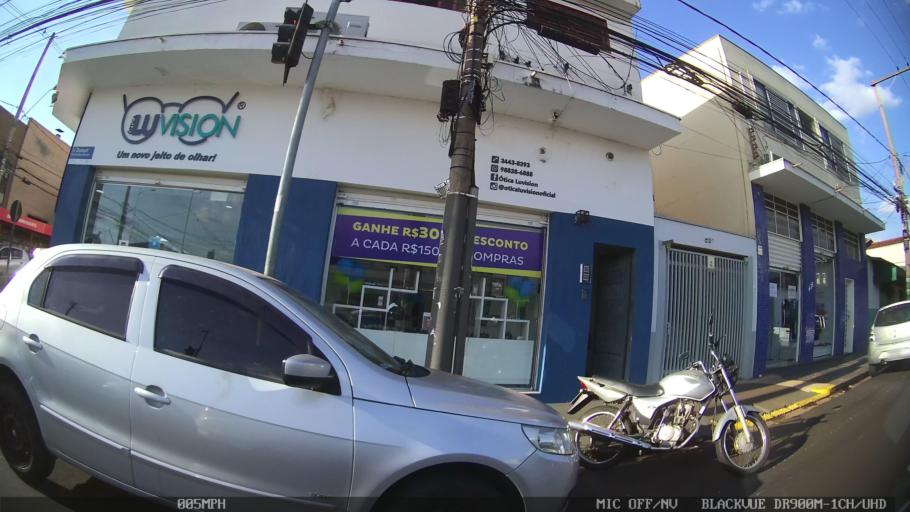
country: BR
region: Sao Paulo
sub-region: Ribeirao Preto
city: Ribeirao Preto
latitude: -21.1796
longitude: -47.7972
